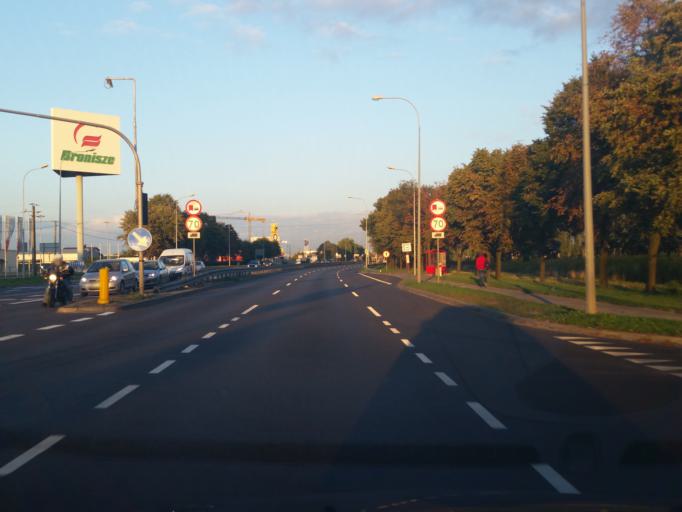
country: PL
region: Masovian Voivodeship
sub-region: Powiat pruszkowski
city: Piastow
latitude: 52.2144
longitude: 20.8397
